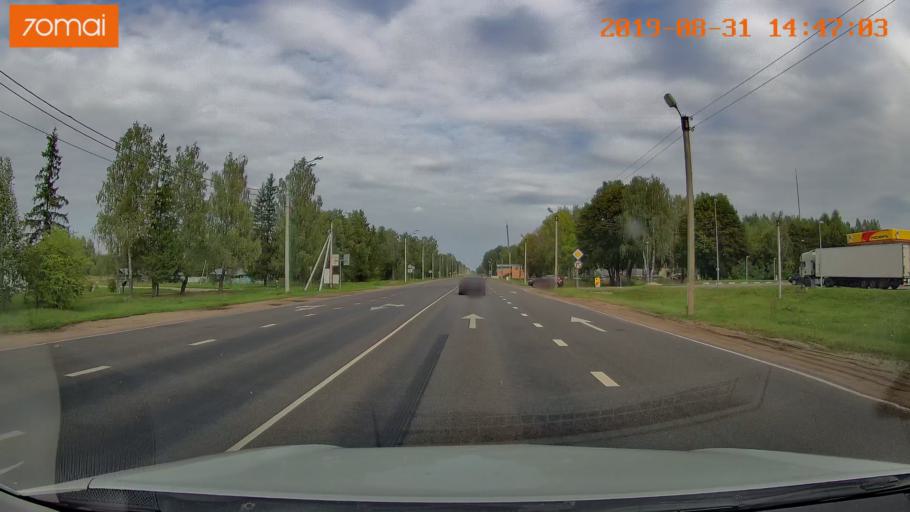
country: RU
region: Kaluga
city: Betlitsa
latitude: 54.2372
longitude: 33.7200
